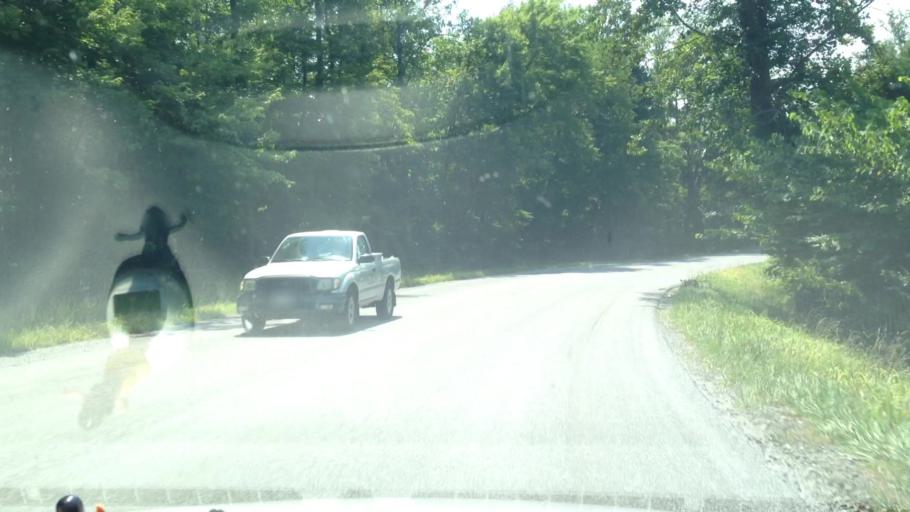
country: US
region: Virginia
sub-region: Patrick County
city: Stuart
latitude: 36.5937
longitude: -80.2907
